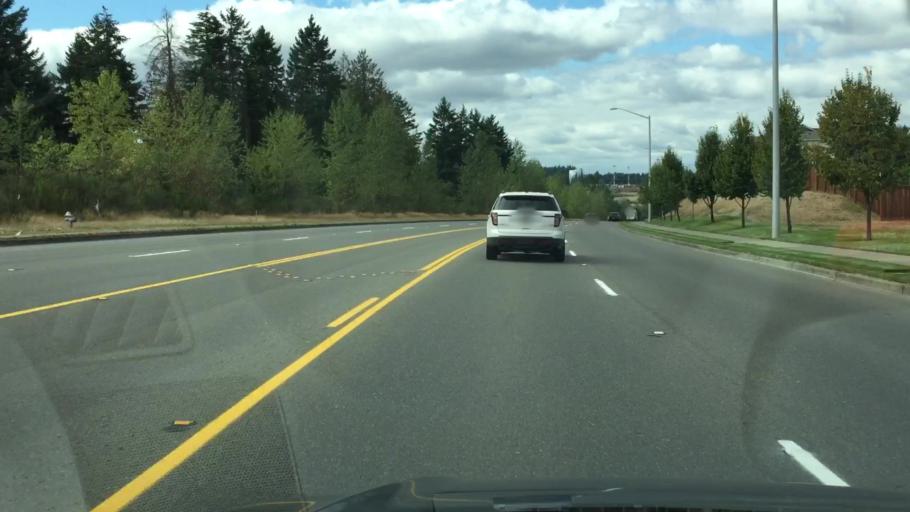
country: US
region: Washington
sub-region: Pierce County
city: South Hill
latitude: 47.0968
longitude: -122.2720
